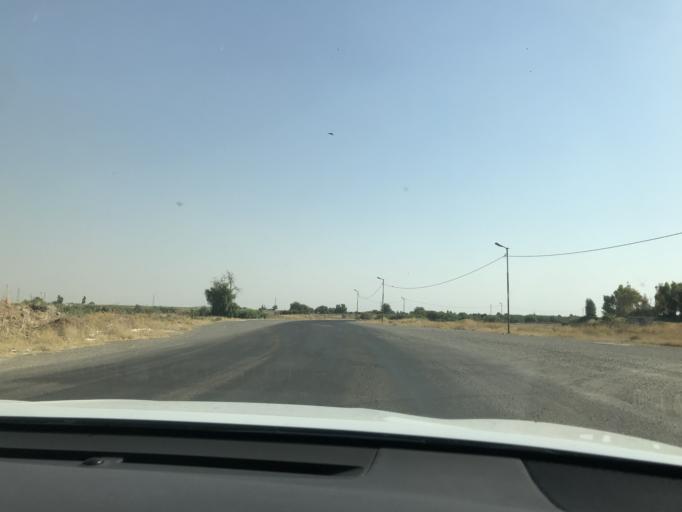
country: IQ
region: Arbil
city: Erbil
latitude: 36.1730
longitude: 43.9240
